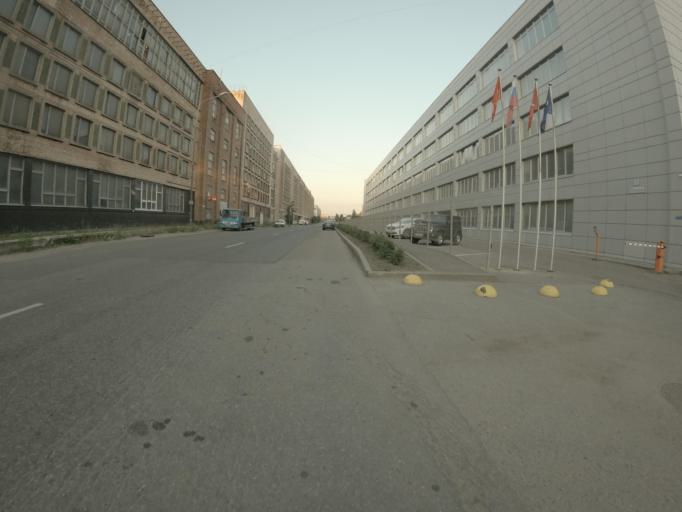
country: RU
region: St.-Petersburg
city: Admiralteisky
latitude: 59.8878
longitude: 30.2822
